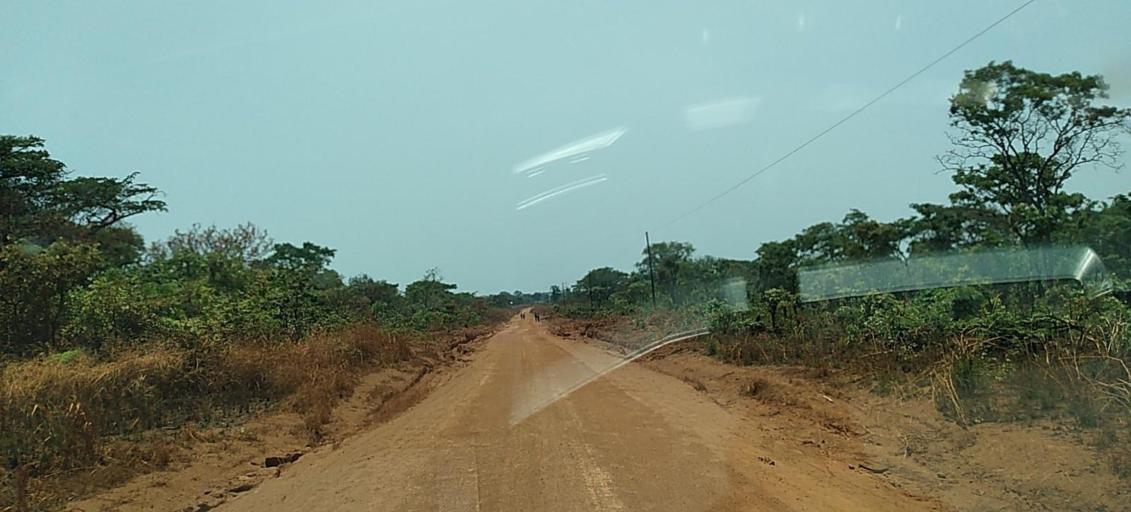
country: CD
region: Katanga
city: Kipushi
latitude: -11.9382
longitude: 26.9535
